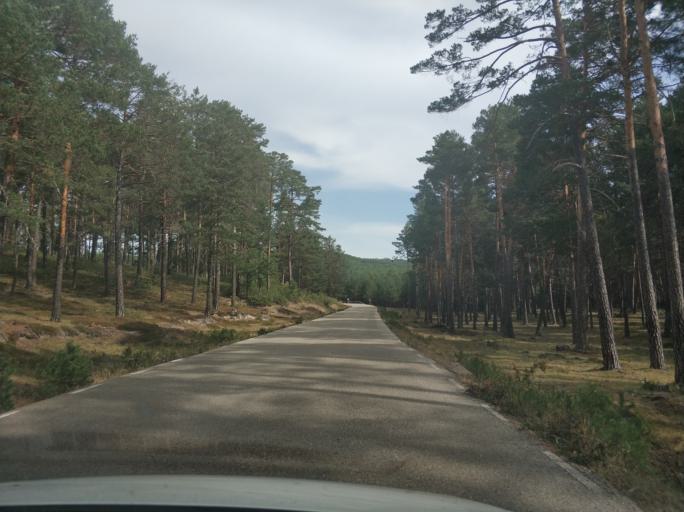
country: ES
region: Castille and Leon
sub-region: Provincia de Soria
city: Navaleno
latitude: 41.8760
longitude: -2.9379
